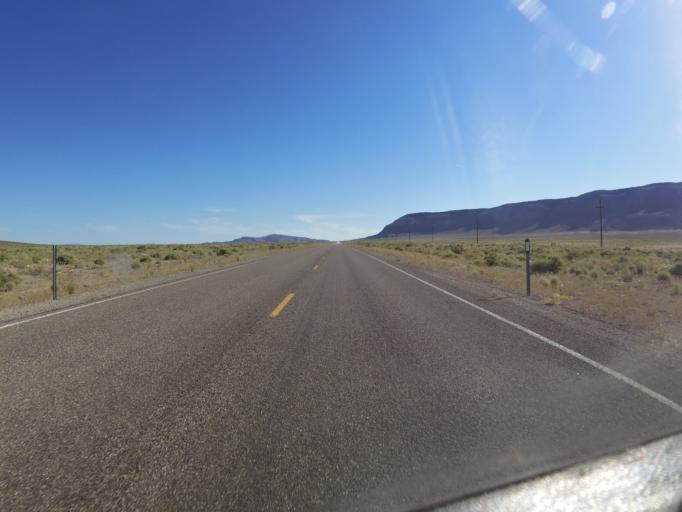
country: US
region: Nevada
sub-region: Nye County
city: Tonopah
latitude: 38.3832
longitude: -116.2177
